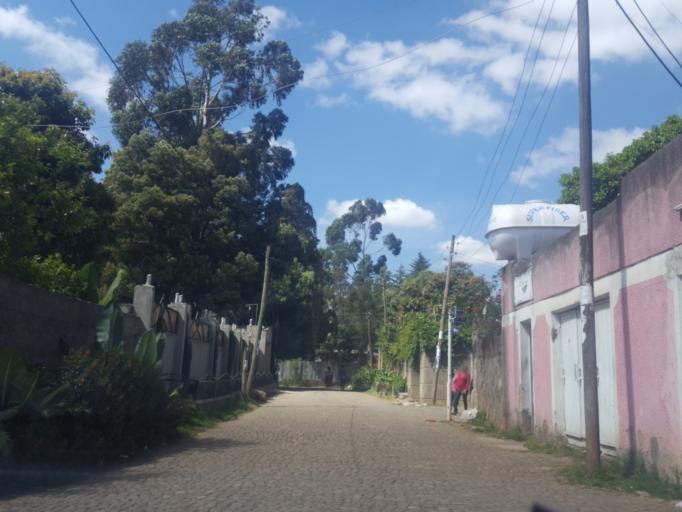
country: ET
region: Adis Abeba
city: Addis Ababa
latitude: 9.0591
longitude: 38.7426
